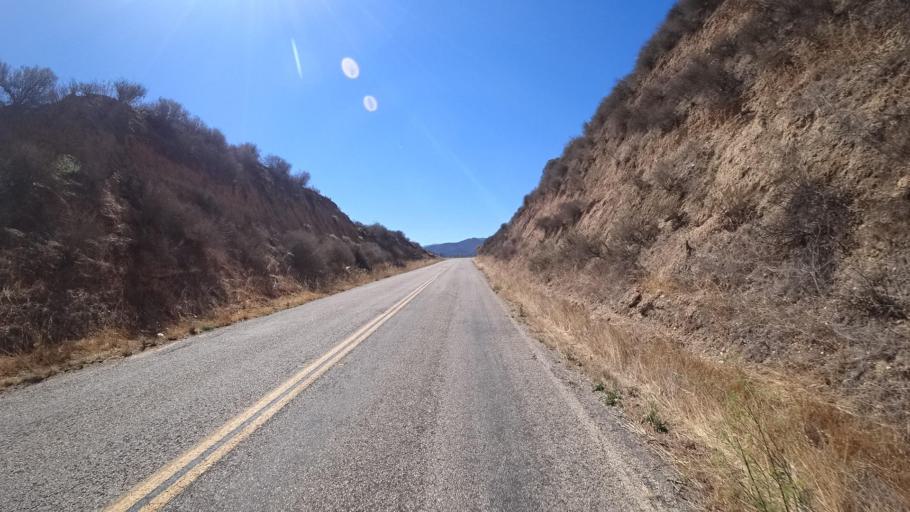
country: US
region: California
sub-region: Monterey County
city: Greenfield
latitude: 36.2716
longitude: -121.3347
